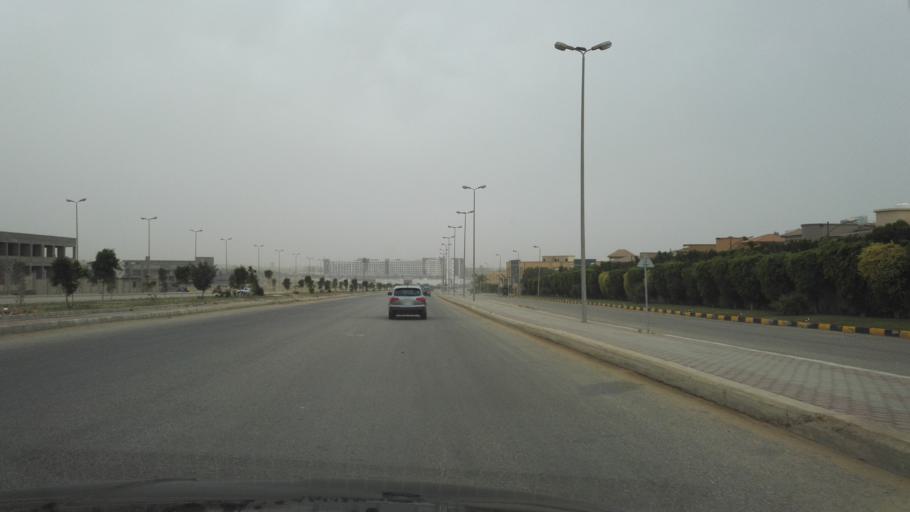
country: EG
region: Muhafazat al Qalyubiyah
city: Al Khankah
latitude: 30.0332
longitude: 31.5089
